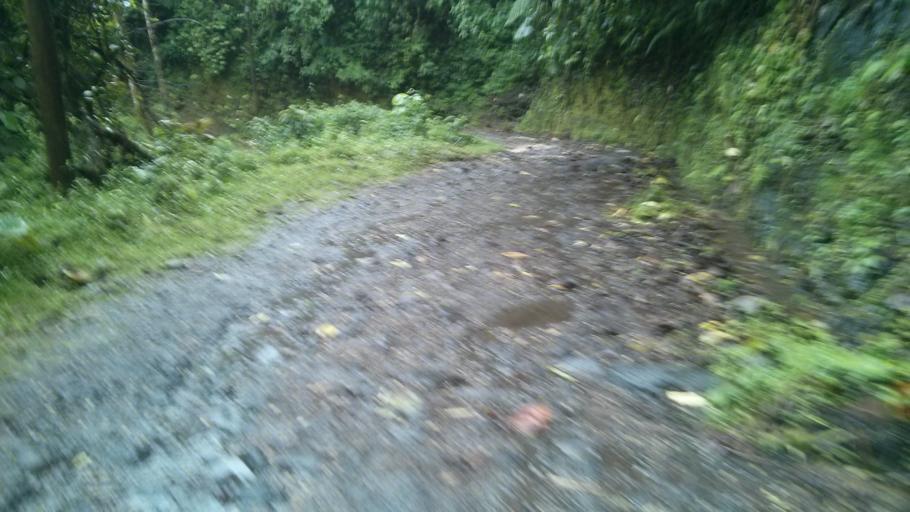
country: CR
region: San Jose
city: Ipis
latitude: 10.0303
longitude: -83.9316
